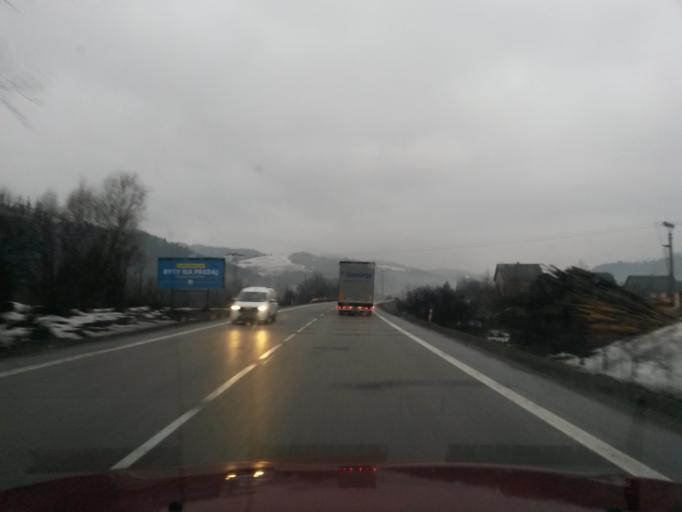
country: SK
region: Zilinsky
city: Kysucke Nove Mesto
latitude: 49.3329
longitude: 18.8083
